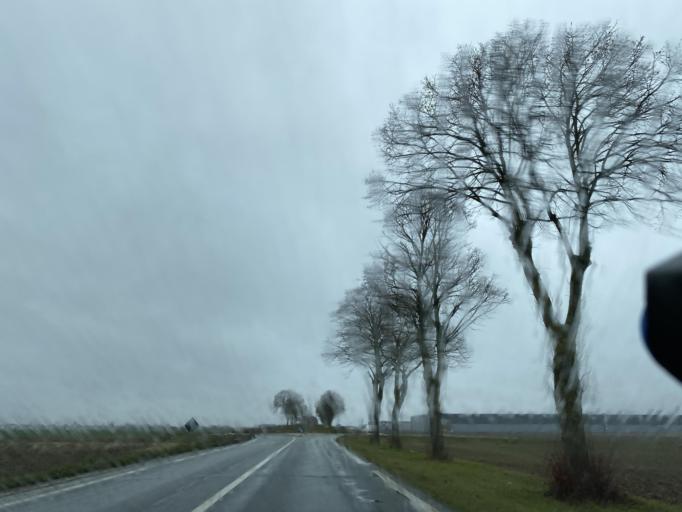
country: FR
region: Centre
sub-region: Departement du Loiret
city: Artenay
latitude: 48.0967
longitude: 1.8650
